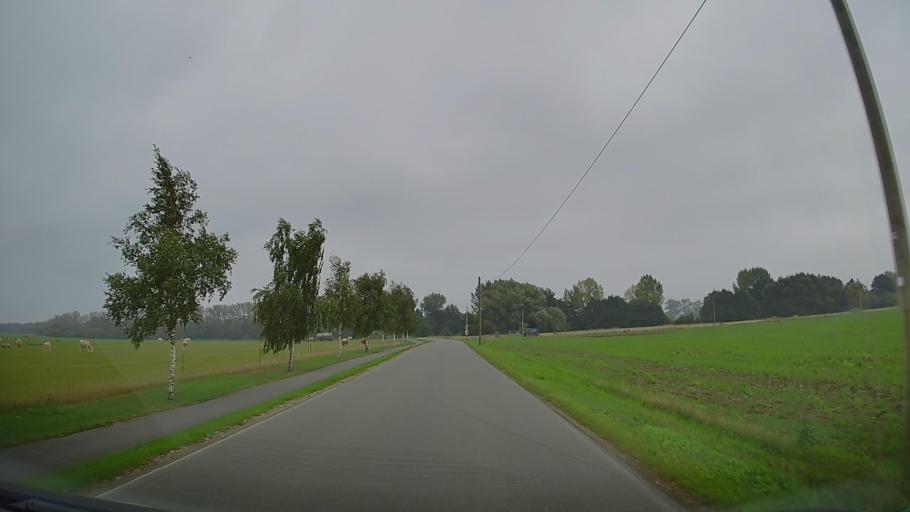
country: DE
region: Mecklenburg-Vorpommern
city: Neubukow
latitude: 54.0579
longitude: 11.6175
